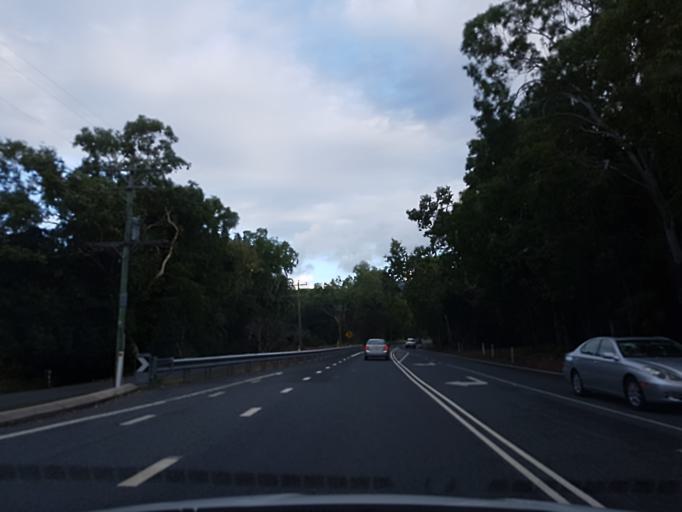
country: AU
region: Queensland
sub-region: Cairns
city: Palm Cove
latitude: -16.6588
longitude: 145.5663
